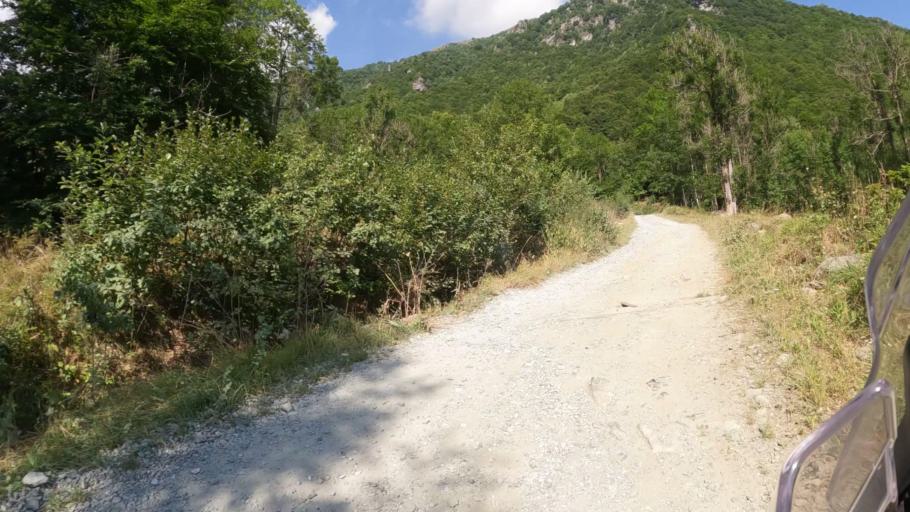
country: IT
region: Piedmont
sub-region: Provincia di Torino
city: Lemie
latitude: 45.2078
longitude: 7.3068
